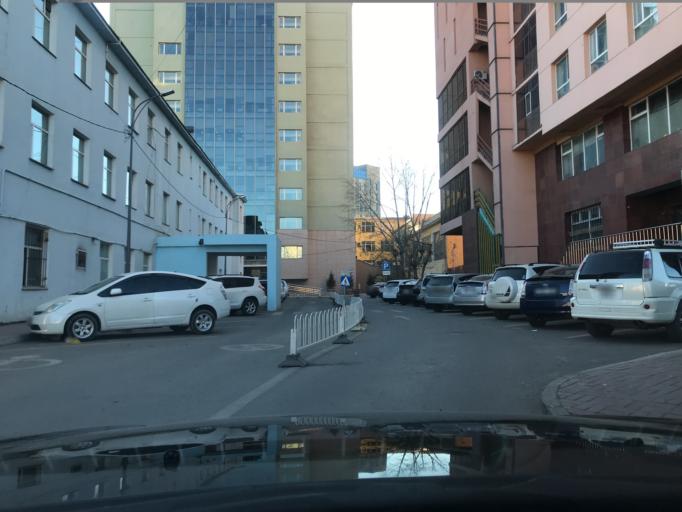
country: MN
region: Ulaanbaatar
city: Ulaanbaatar
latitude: 47.9235
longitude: 106.9149
